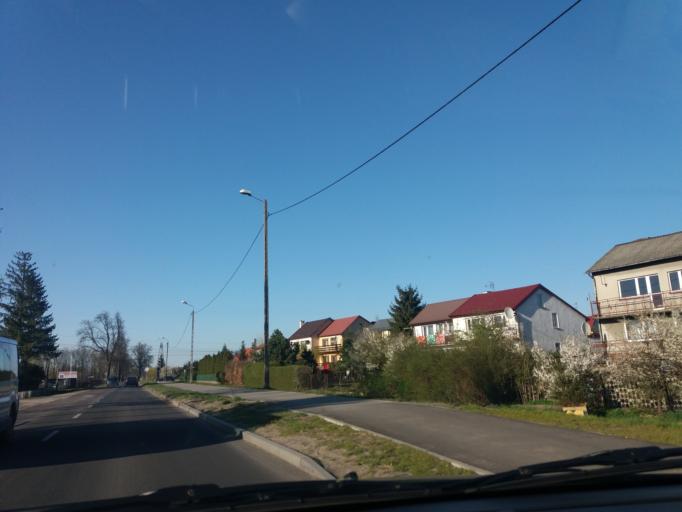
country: PL
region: Warmian-Masurian Voivodeship
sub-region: Powiat nidzicki
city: Nidzica
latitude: 53.3740
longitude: 20.4296
